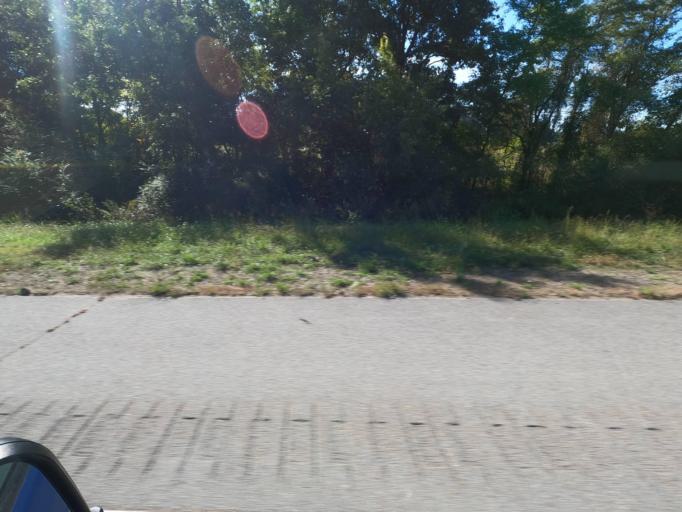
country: US
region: Tennessee
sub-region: Shelby County
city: Lakeland
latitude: 35.3106
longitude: -89.7697
